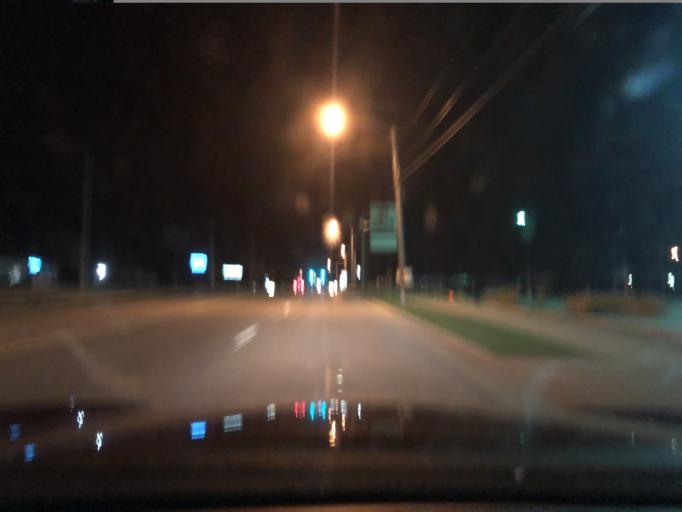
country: US
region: Ohio
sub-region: Logan County
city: Bellefontaine
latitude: 40.3354
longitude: -83.7617
